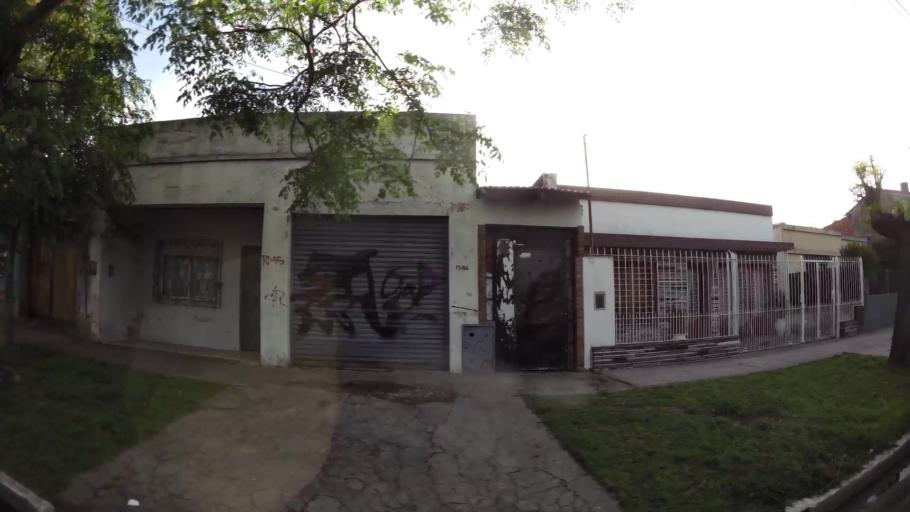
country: AR
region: Buenos Aires
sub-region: Partido de Almirante Brown
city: Adrogue
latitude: -34.7914
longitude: -58.3547
